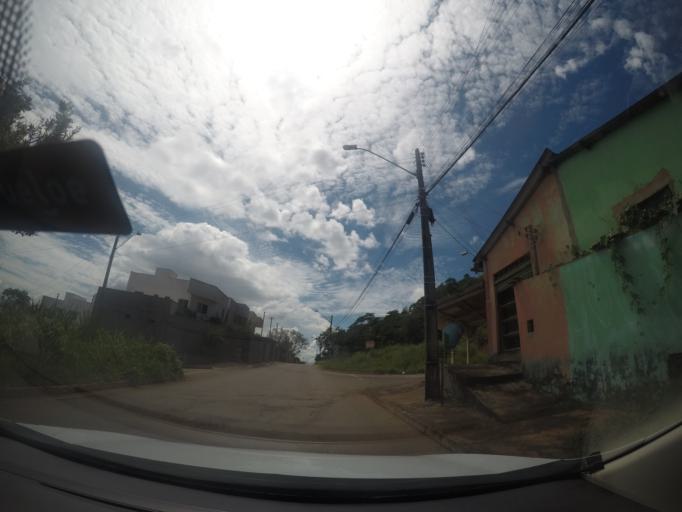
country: BR
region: Goias
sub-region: Goiania
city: Goiania
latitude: -16.6612
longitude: -49.3462
